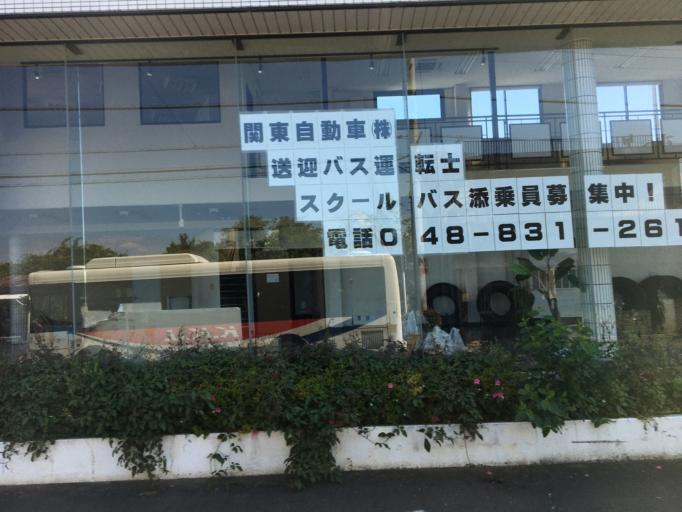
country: JP
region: Saitama
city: Sakado
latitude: 35.9637
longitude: 139.3592
